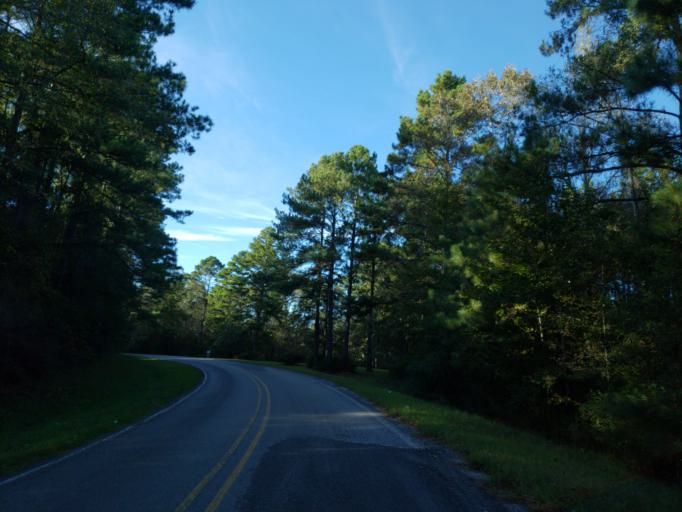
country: US
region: Mississippi
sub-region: Perry County
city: Richton
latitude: 31.3455
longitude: -88.8087
